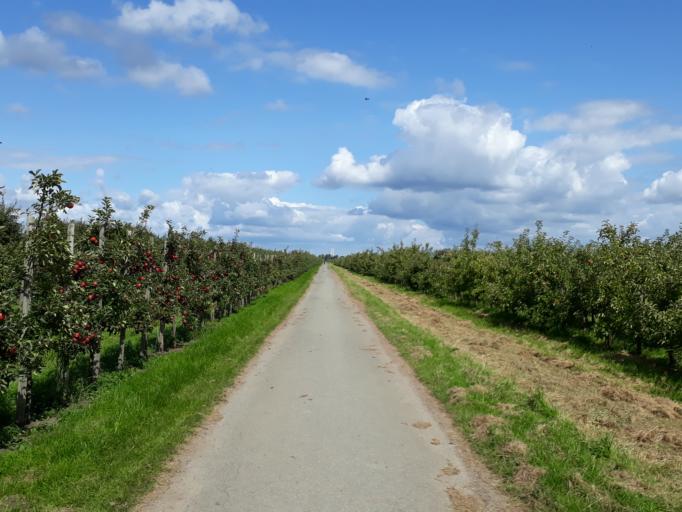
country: DE
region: Lower Saxony
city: Jork
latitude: 53.5002
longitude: 9.6826
